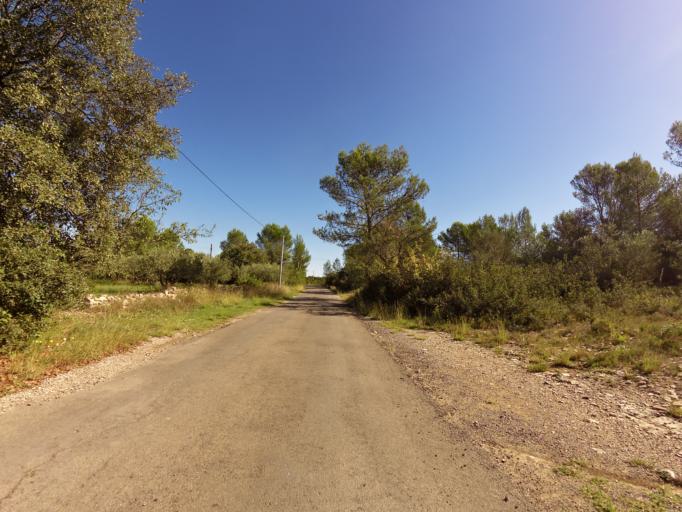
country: FR
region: Languedoc-Roussillon
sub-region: Departement de l'Herault
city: Villetelle
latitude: 43.7438
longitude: 4.1331
